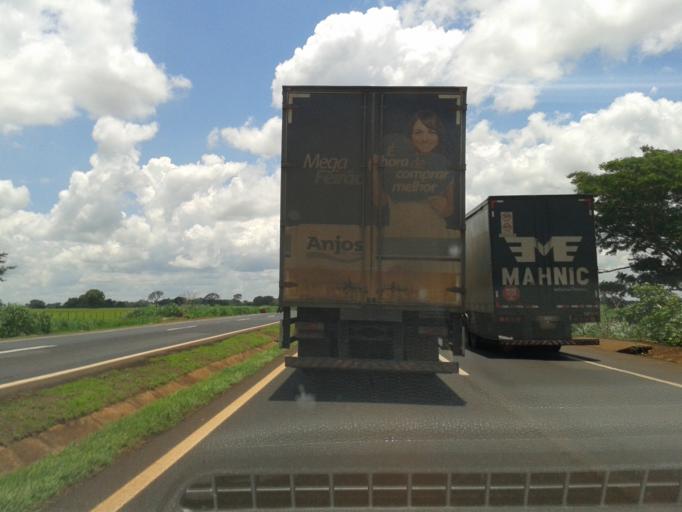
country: BR
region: Minas Gerais
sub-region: Centralina
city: Centralina
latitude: -18.6467
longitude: -49.1749
